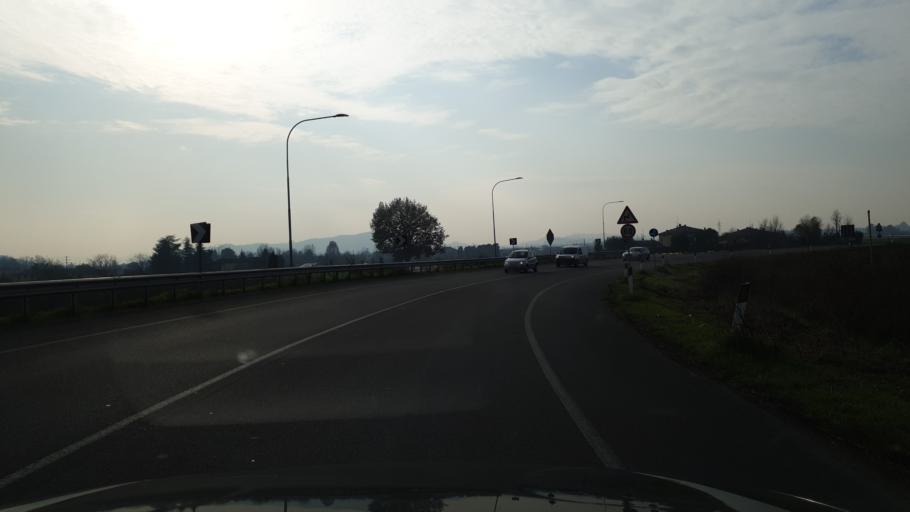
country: IT
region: Emilia-Romagna
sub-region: Provincia di Bologna
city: Crespellano
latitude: 44.5153
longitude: 11.1133
